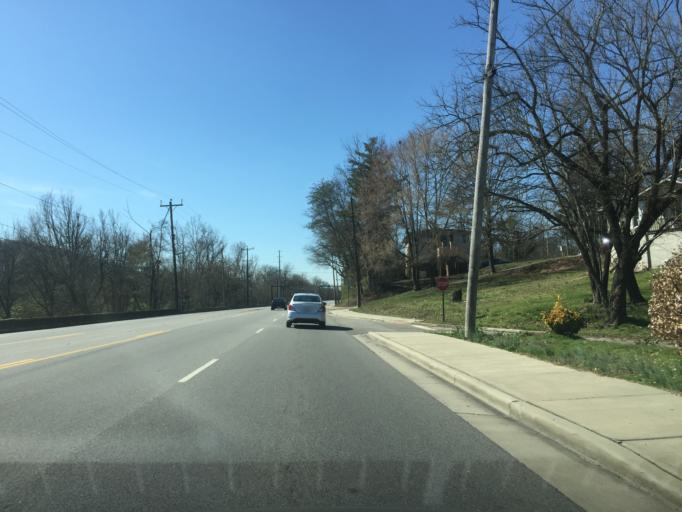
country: US
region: Tennessee
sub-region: Hamilton County
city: Red Bank
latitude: 35.1003
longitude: -85.3024
